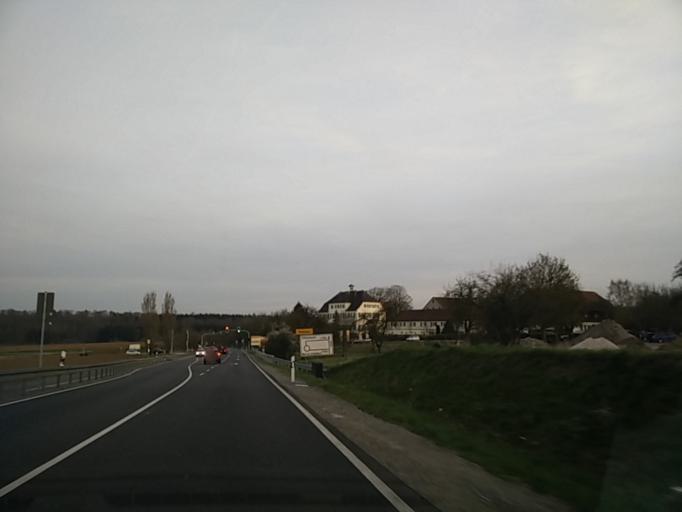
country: DE
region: Baden-Wuerttemberg
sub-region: Regierungsbezirk Stuttgart
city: Holzgerlingen
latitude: 48.6171
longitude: 9.0239
